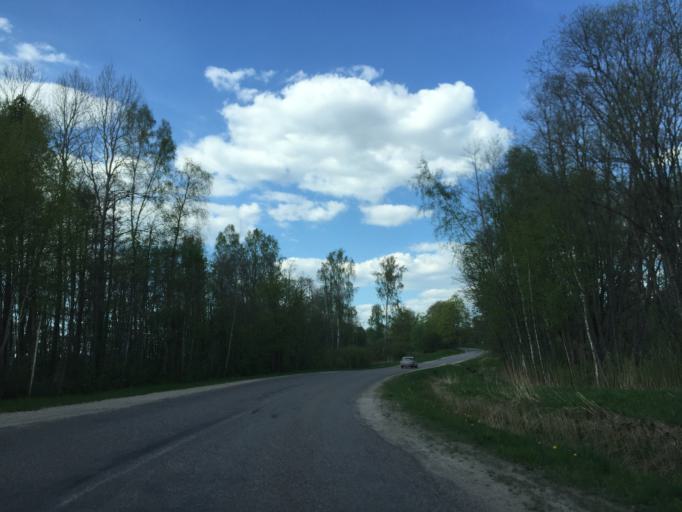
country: LV
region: Limbazu Rajons
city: Limbazi
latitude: 57.4749
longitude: 24.7107
